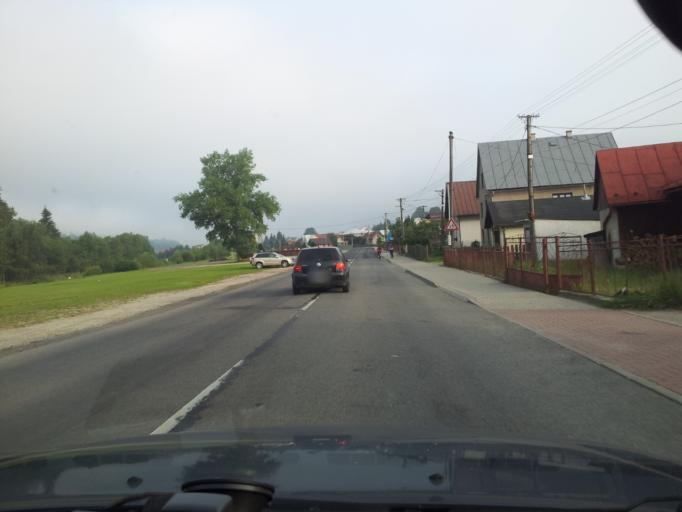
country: SK
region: Zilinsky
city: Cadca
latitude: 49.3759
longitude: 18.8906
